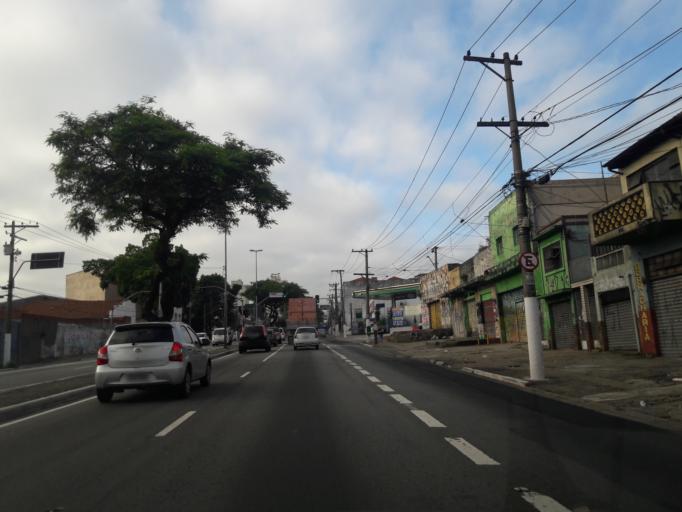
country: BR
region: Sao Paulo
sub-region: Sao Caetano Do Sul
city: Sao Caetano do Sul
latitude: -23.6086
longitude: -46.5997
